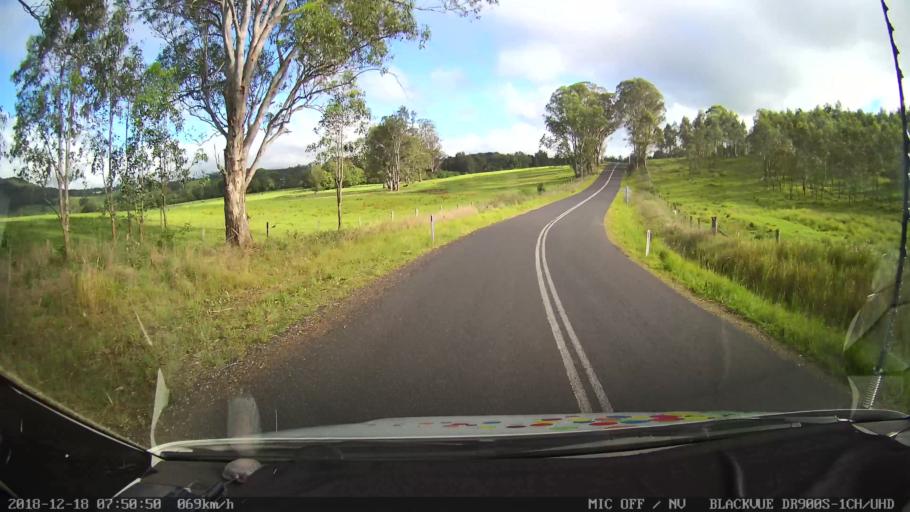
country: AU
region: New South Wales
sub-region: Kyogle
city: Kyogle
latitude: -28.4418
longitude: 152.5743
